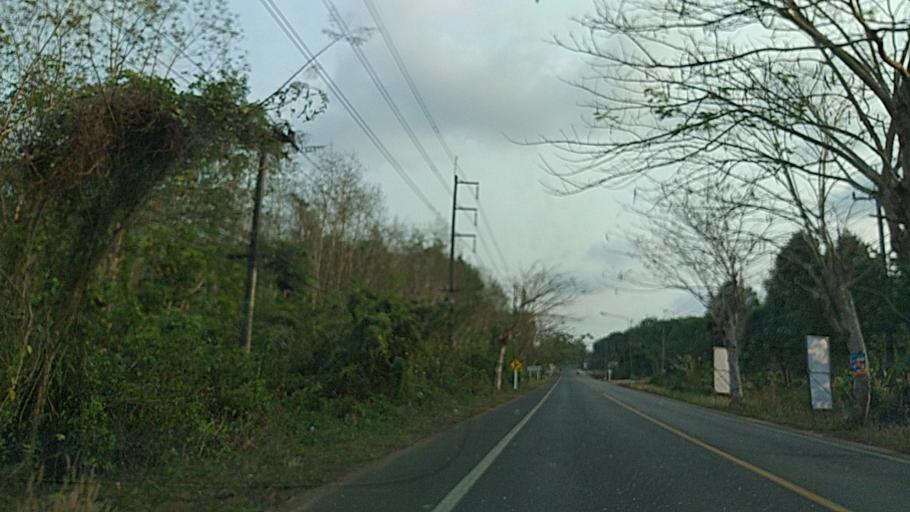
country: TH
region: Trat
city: Laem Ngop
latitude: 12.2741
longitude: 102.3056
